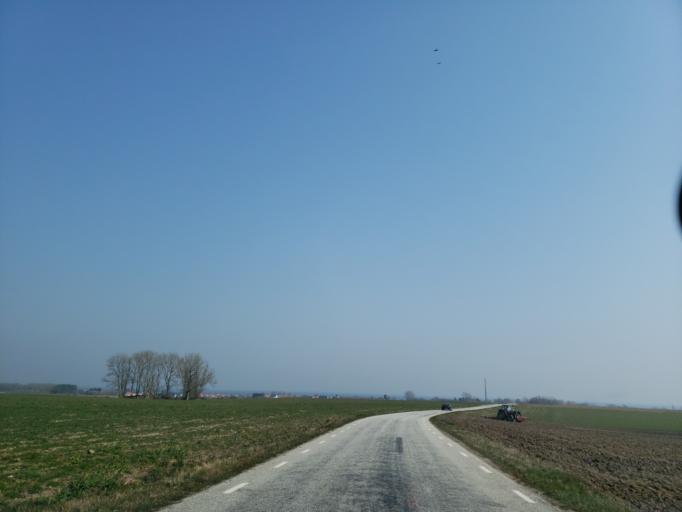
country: SE
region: Skane
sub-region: Simrishamns Kommun
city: Simrishamn
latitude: 55.5112
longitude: 14.3268
